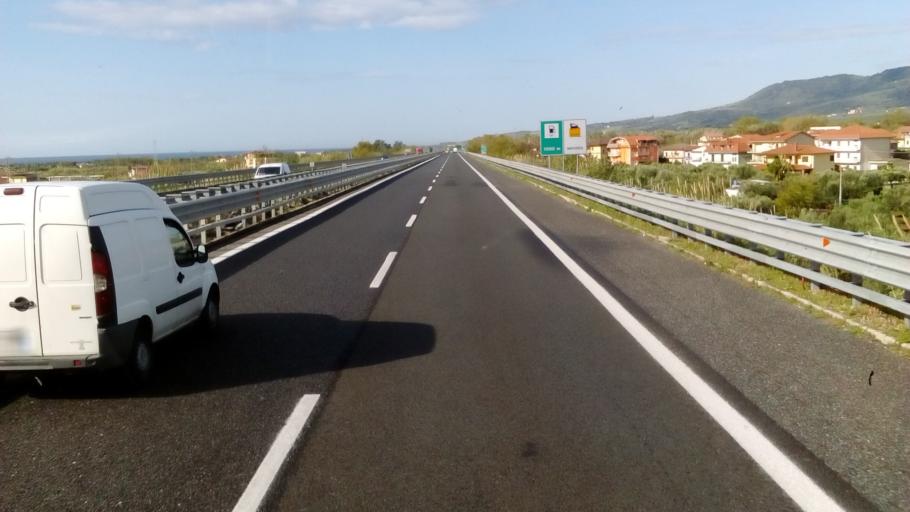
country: IT
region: Calabria
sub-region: Provincia di Catanzaro
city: Santa Eufemia Lamezia
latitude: 38.9264
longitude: 16.2496
